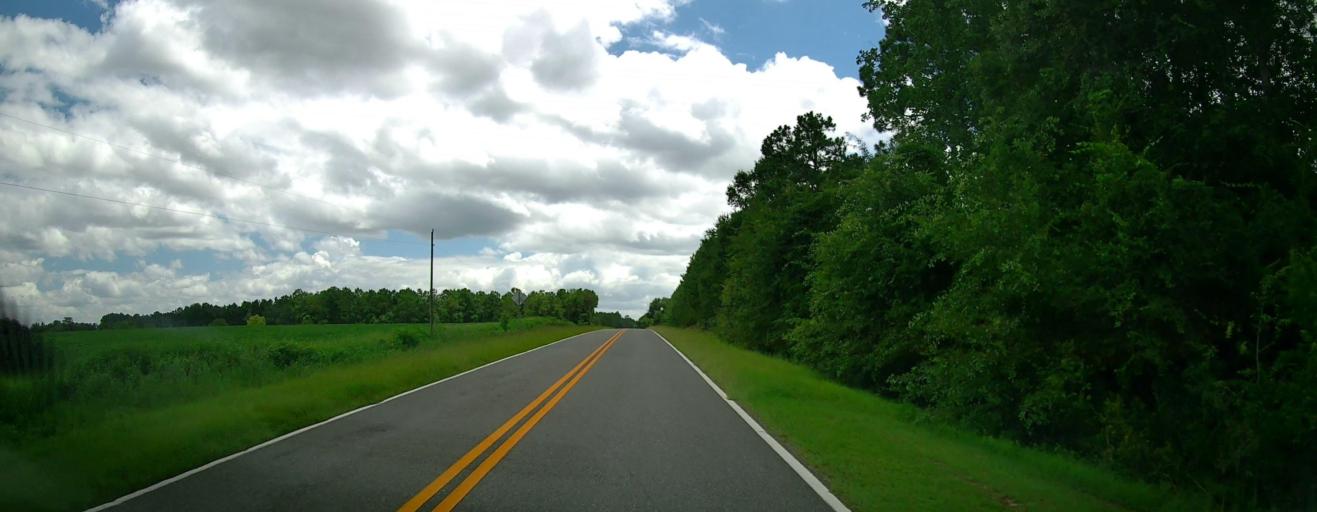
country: US
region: Georgia
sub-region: Turner County
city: Ashburn
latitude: 31.6902
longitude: -83.4761
